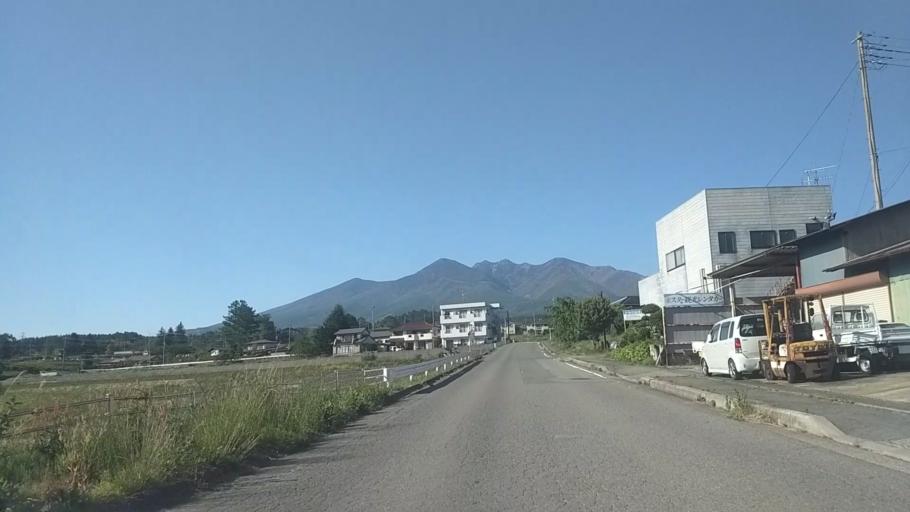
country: JP
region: Nagano
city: Chino
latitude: 35.8660
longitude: 138.3127
